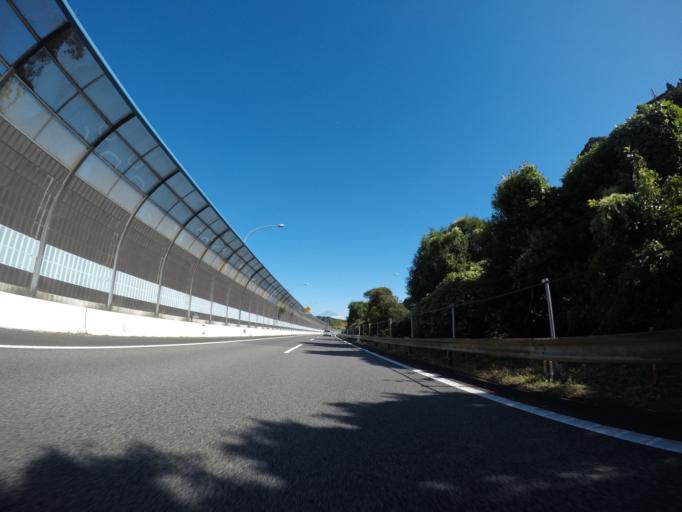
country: JP
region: Shizuoka
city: Yaizu
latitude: 34.9208
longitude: 138.3472
